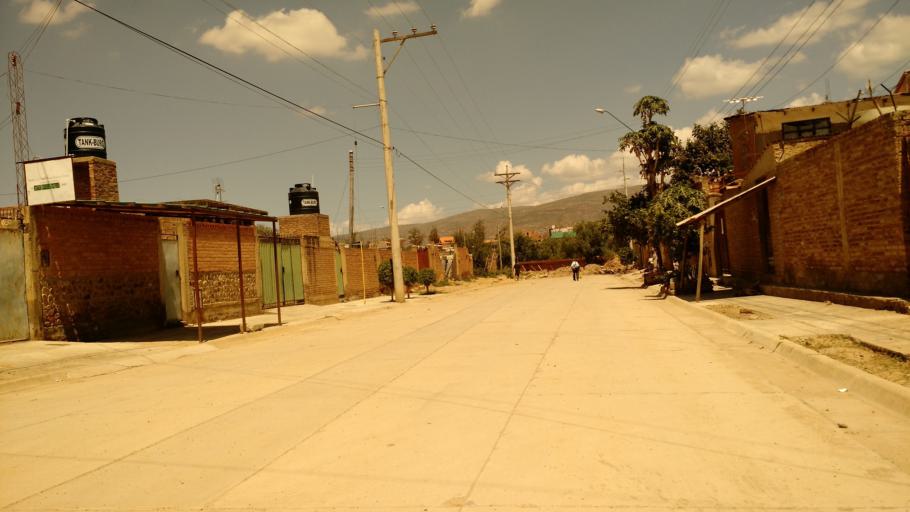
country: BO
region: Cochabamba
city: Cochabamba
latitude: -17.4411
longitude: -66.1536
